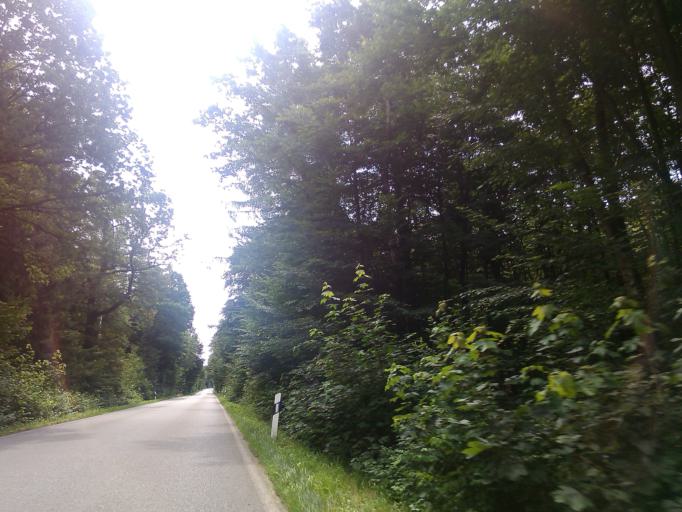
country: DE
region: Bavaria
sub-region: Upper Bavaria
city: Gauting
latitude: 48.0797
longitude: 11.3525
